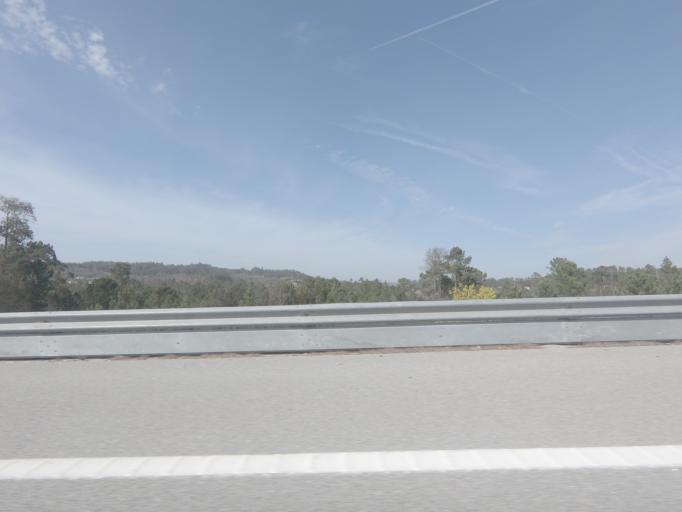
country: PT
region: Viseu
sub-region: Viseu
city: Abraveses
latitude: 40.6335
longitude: -7.9832
